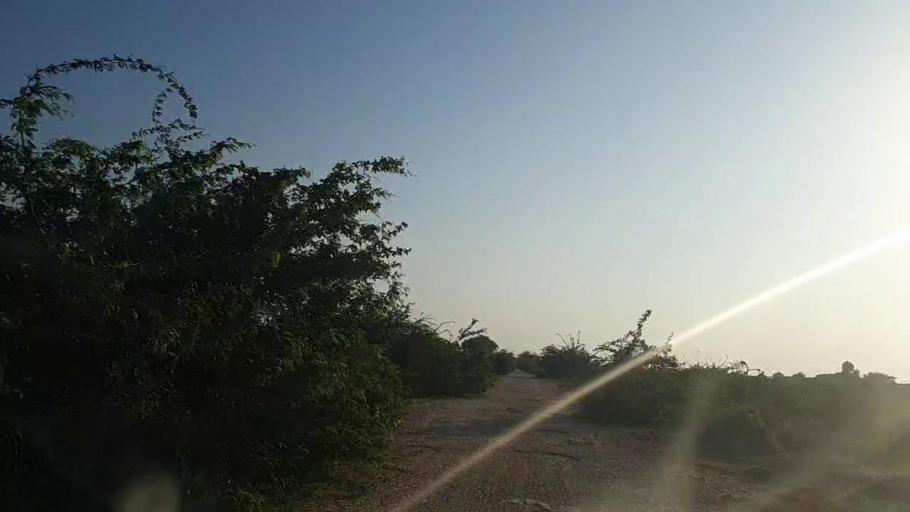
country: PK
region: Sindh
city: Jati
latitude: 24.4238
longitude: 68.1874
